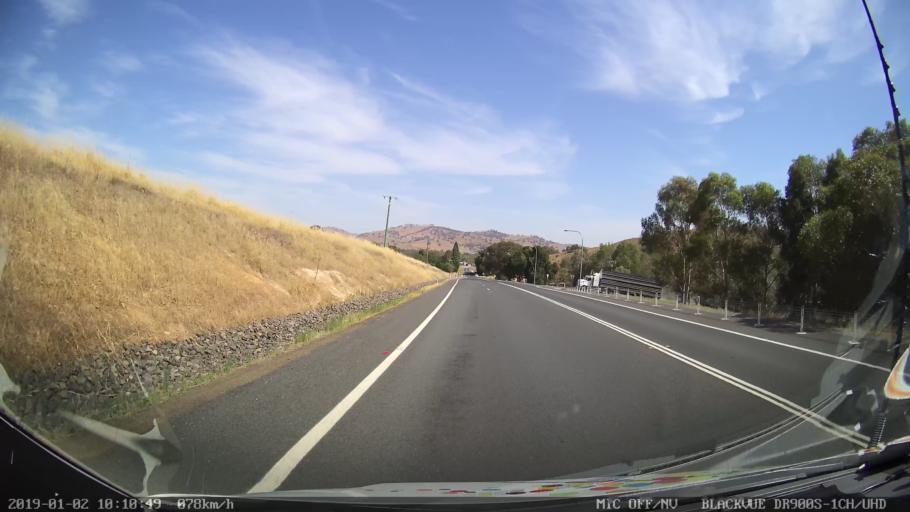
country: AU
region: New South Wales
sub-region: Gundagai
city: Gundagai
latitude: -35.0994
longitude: 148.0952
